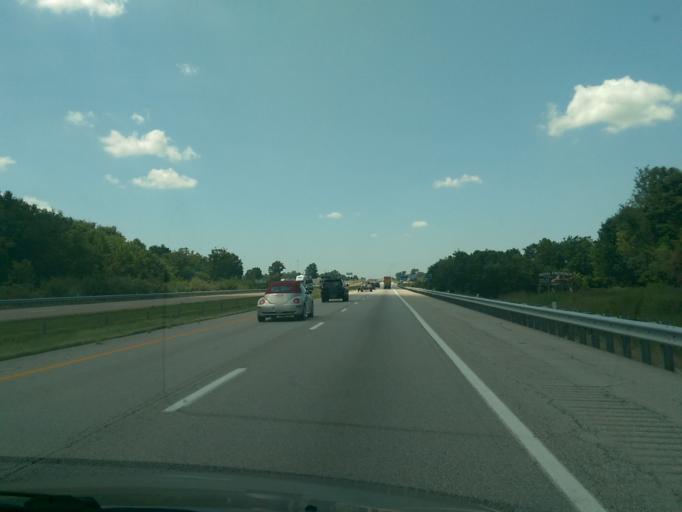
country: US
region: Missouri
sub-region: Cooper County
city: Boonville
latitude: 38.9371
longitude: -92.7216
